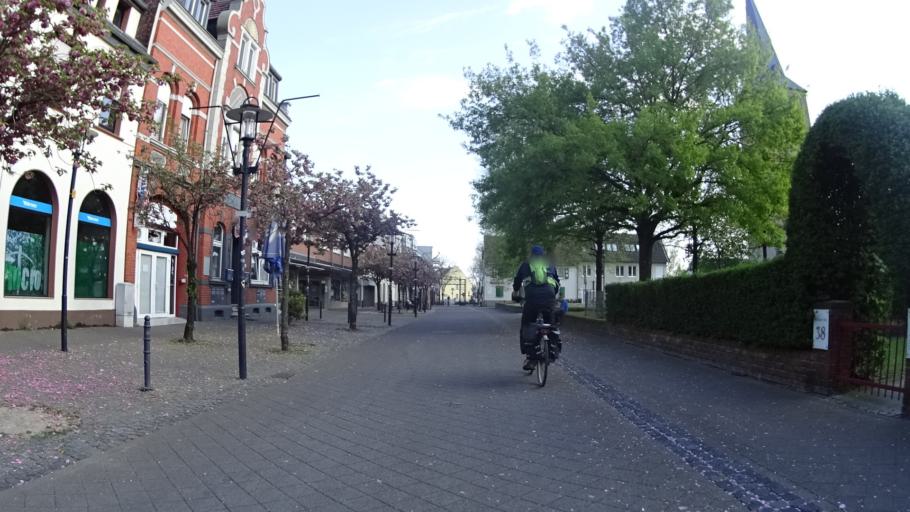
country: DE
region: North Rhine-Westphalia
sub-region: Regierungsbezirk Dusseldorf
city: Dormagen
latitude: 51.0916
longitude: 6.8433
